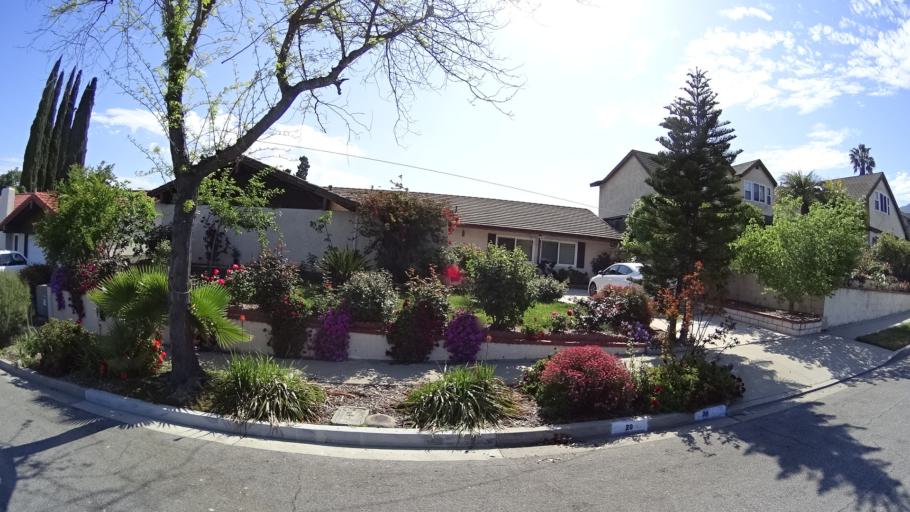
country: US
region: California
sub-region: Ventura County
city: Casa Conejo
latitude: 34.1784
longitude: -118.9237
